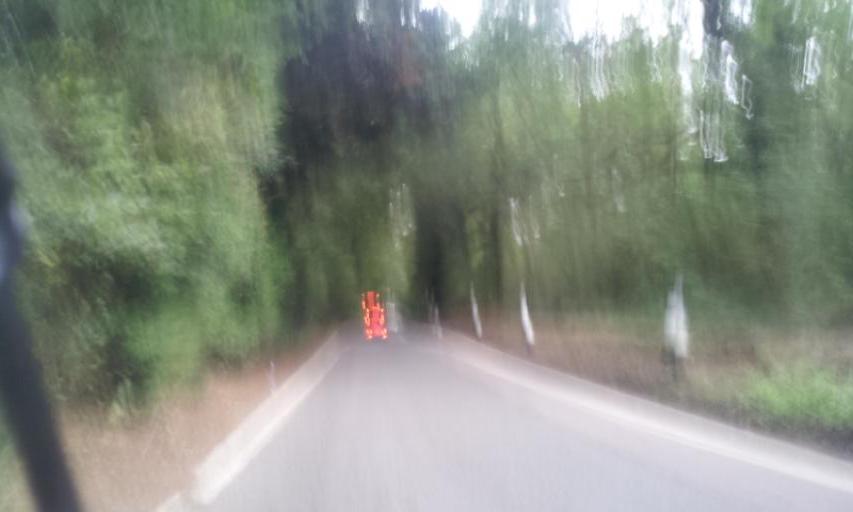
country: GB
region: England
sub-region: Kent
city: Tonbridge
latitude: 51.2261
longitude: 0.2973
